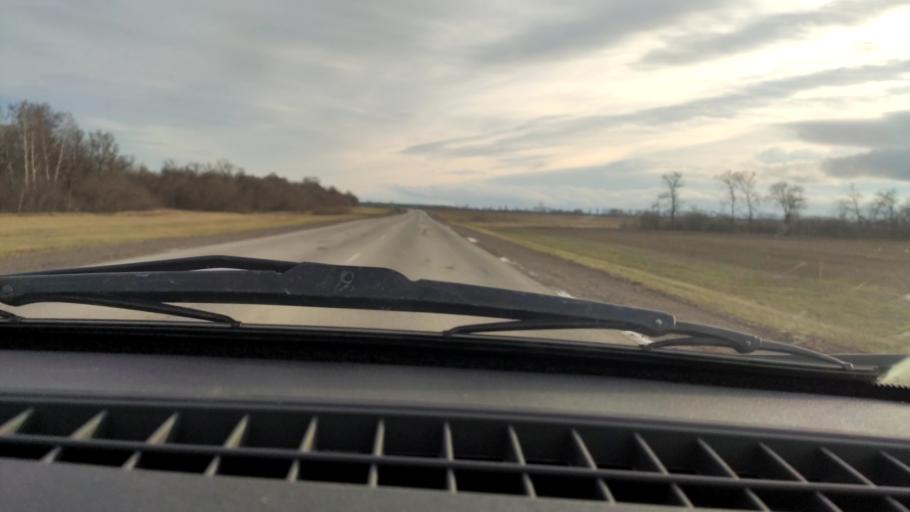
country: RU
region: Bashkortostan
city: Davlekanovo
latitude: 54.2816
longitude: 55.1098
